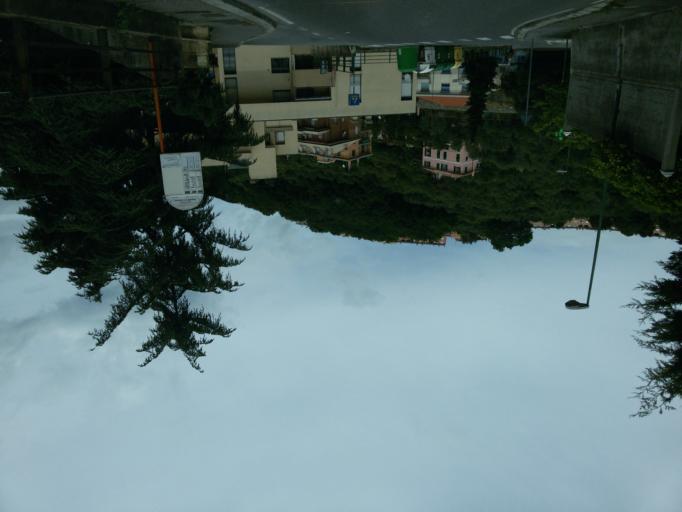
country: IT
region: Liguria
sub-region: Provincia di Genova
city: Piccarello
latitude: 44.4397
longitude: 8.9766
